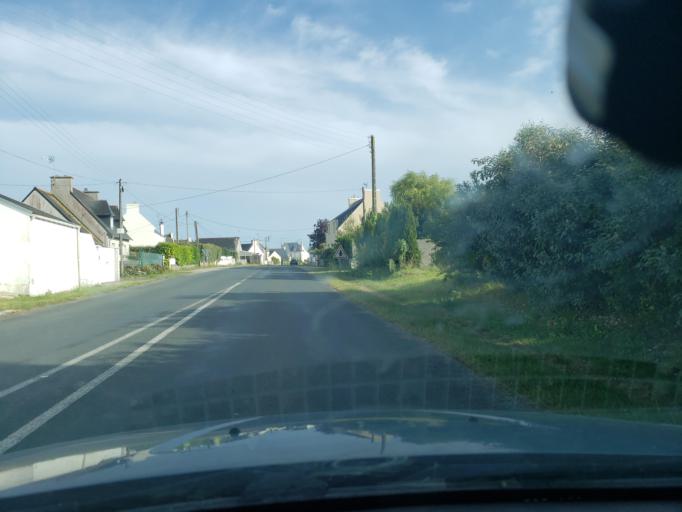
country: FR
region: Brittany
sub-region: Departement du Finistere
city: Guilvinec
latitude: 47.8081
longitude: -4.2812
